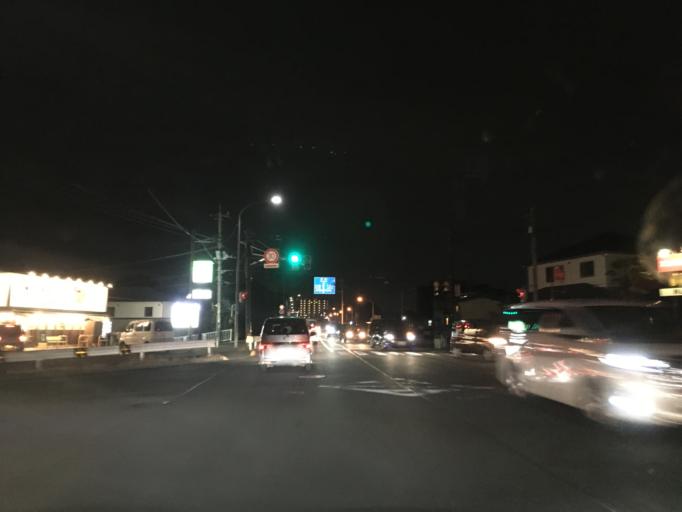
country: JP
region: Saitama
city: Sayama
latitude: 35.8614
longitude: 139.4017
